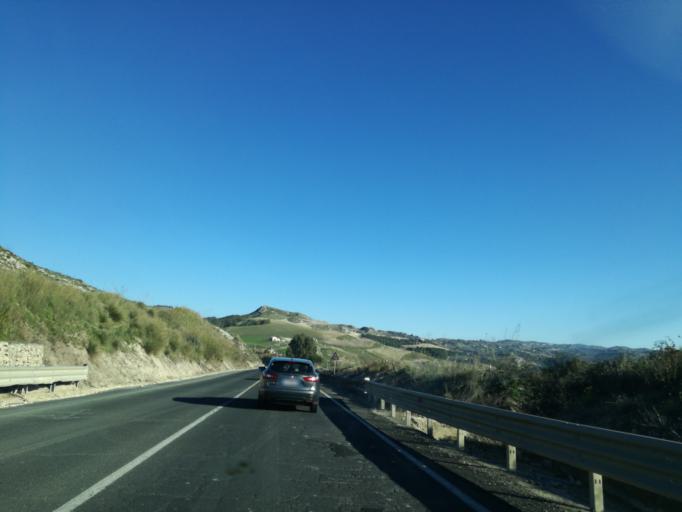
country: IT
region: Sicily
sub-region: Catania
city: San Michele di Ganzaria
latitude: 37.2335
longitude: 14.4486
